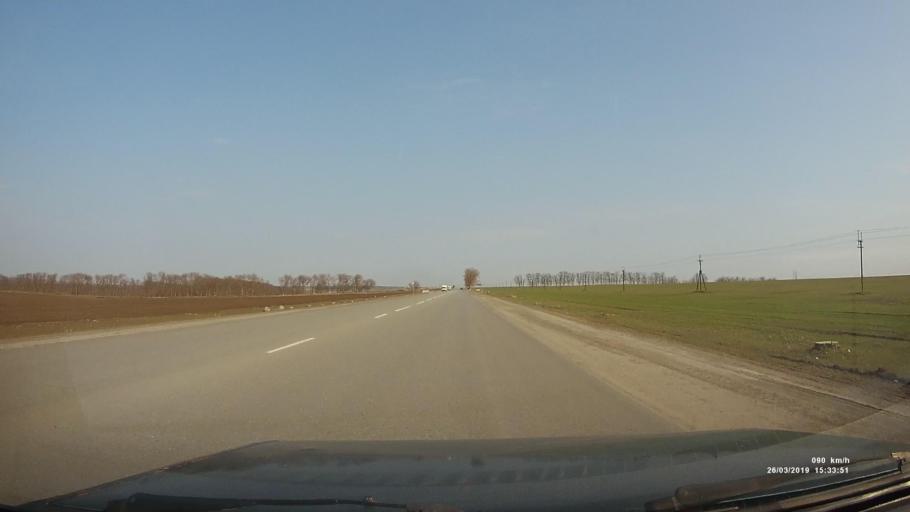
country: RU
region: Rostov
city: Sinyavskoye
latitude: 47.3013
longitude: 39.1819
